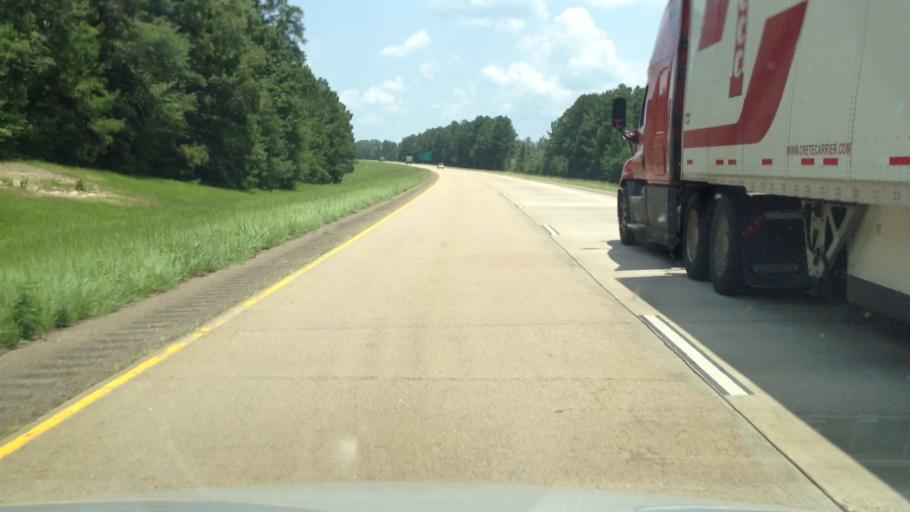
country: US
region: Louisiana
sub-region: Rapides Parish
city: Lecompte
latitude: 31.0347
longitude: -92.4125
